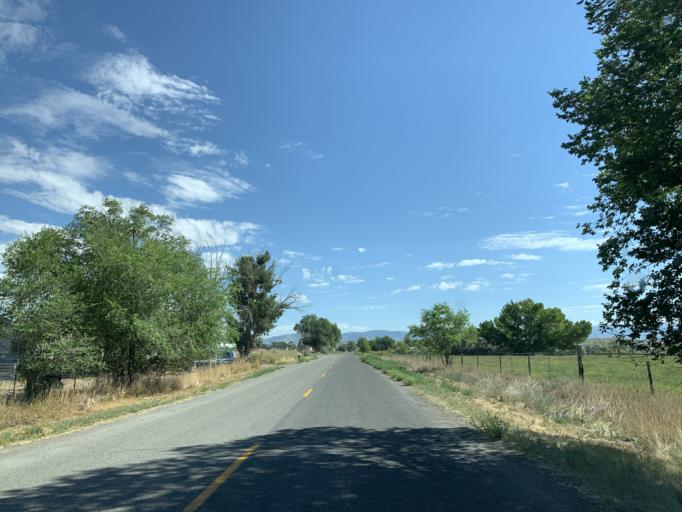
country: US
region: Utah
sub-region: Carbon County
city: Wellington
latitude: 39.5449
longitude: -110.6866
